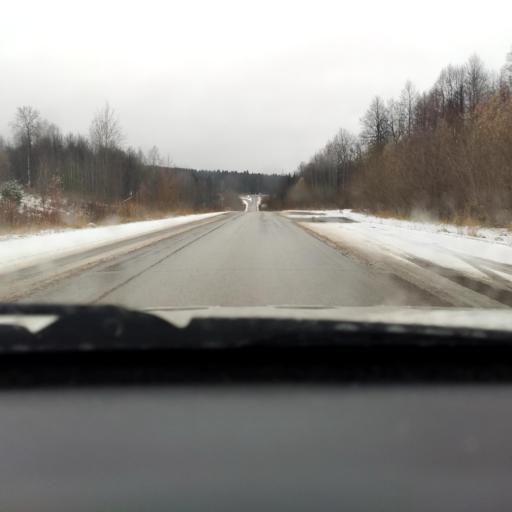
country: RU
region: Perm
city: Ferma
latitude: 57.9772
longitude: 56.3530
